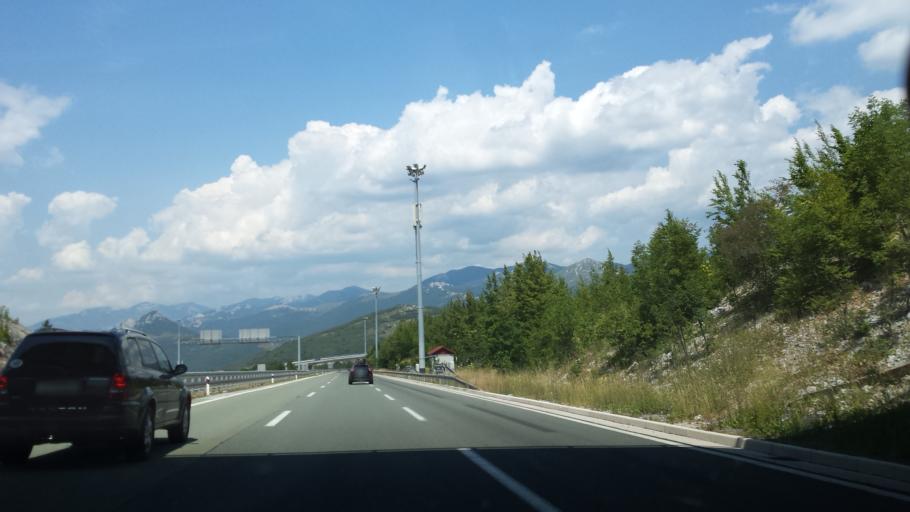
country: HR
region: Primorsko-Goranska
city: Krasica
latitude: 45.3344
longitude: 14.5967
